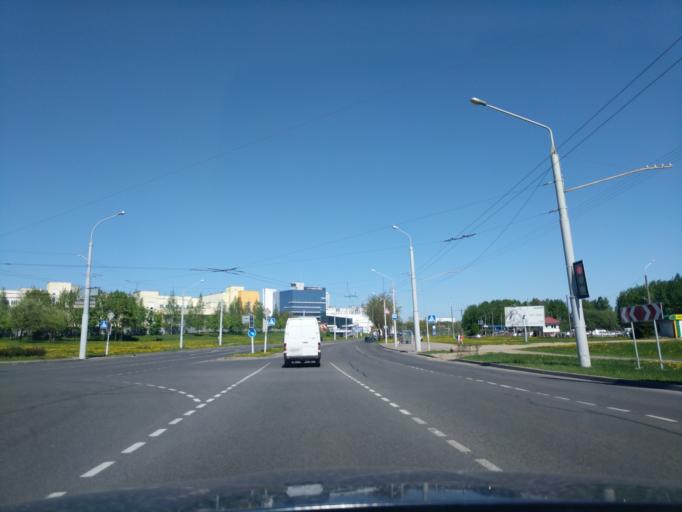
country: BY
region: Minsk
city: Novoye Medvezhino
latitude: 53.8902
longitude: 27.4555
